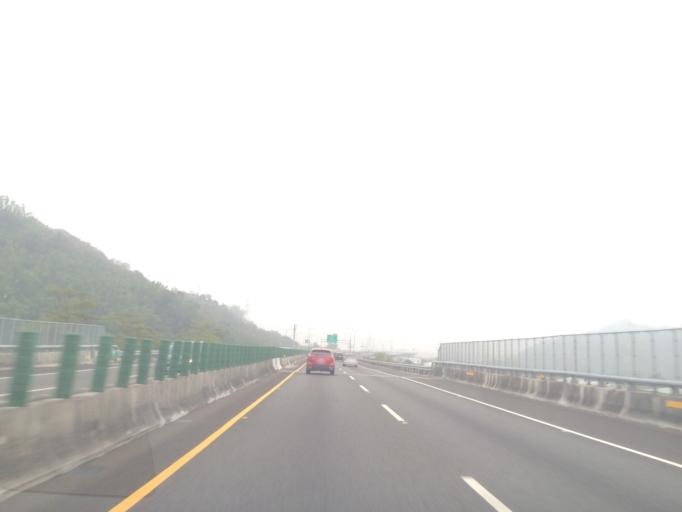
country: TW
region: Taiwan
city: Zhongxing New Village
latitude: 24.0129
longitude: 120.6955
